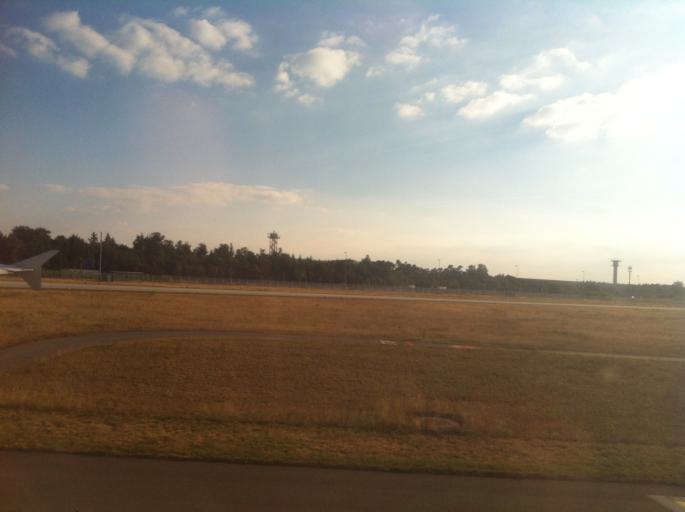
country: DE
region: Hesse
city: Kelsterbach
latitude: 50.0438
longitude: 8.5297
